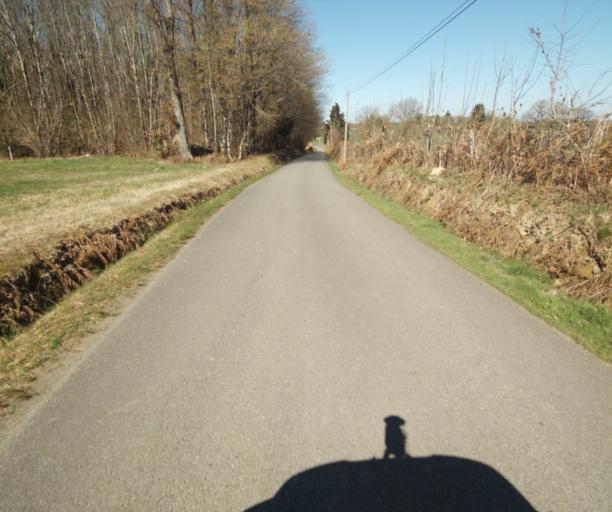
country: FR
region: Limousin
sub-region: Departement de la Correze
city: Saint-Clement
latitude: 45.3109
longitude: 1.6851
